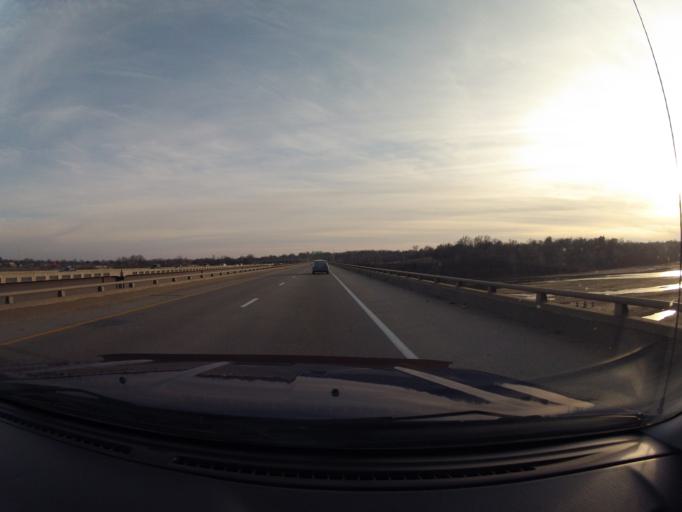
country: US
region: Kansas
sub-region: Shawnee County
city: Topeka
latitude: 39.0722
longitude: -95.7316
